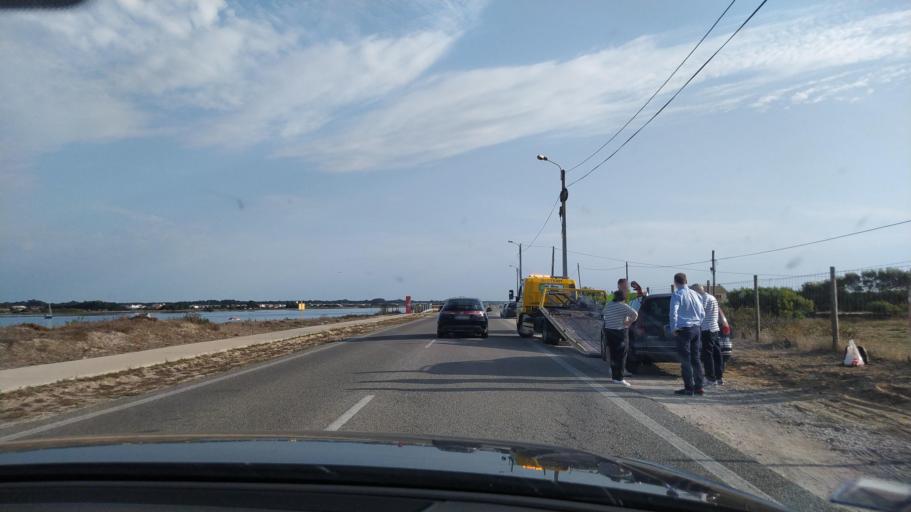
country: PT
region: Aveiro
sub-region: Ilhavo
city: Gafanha da Encarnacao
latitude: 40.6042
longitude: -8.7487
